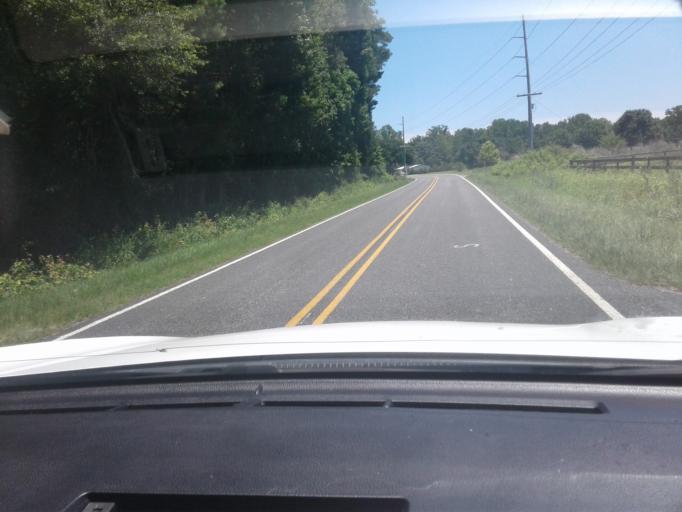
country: US
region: North Carolina
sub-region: Harnett County
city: Walkertown
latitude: 35.3391
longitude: -78.9132
